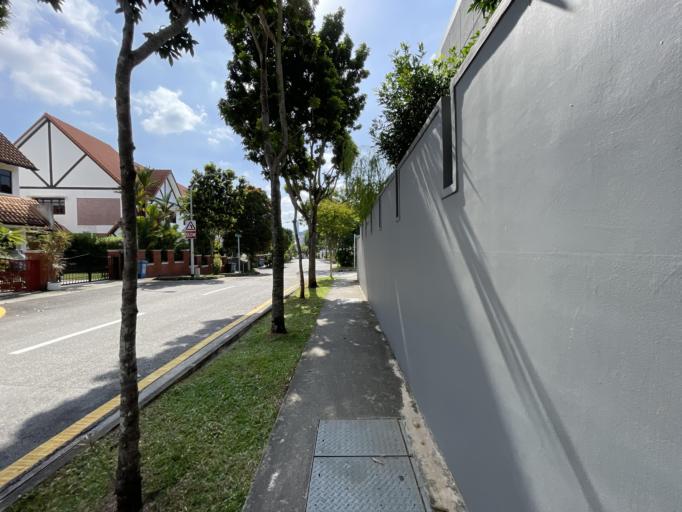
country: SG
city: Singapore
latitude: 1.2808
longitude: 103.7875
